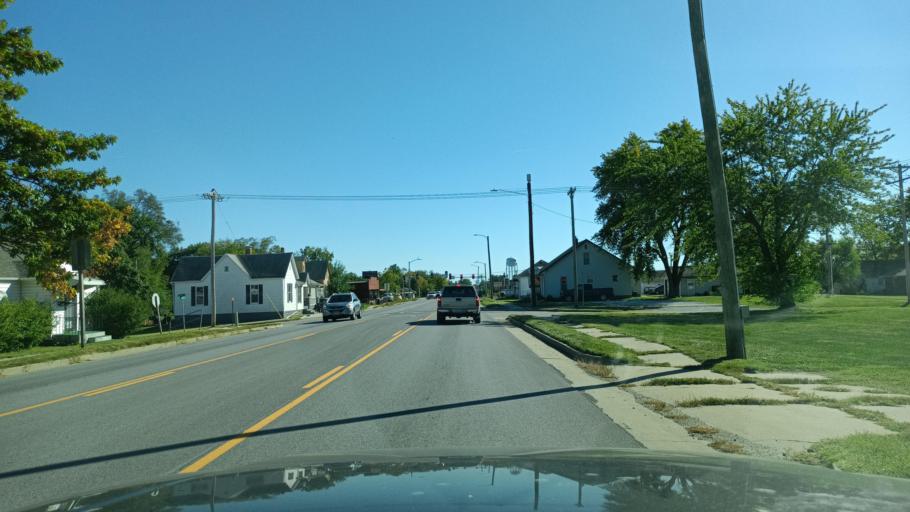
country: US
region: Missouri
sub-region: Macon County
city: Macon
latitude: 39.7393
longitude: -92.4653
